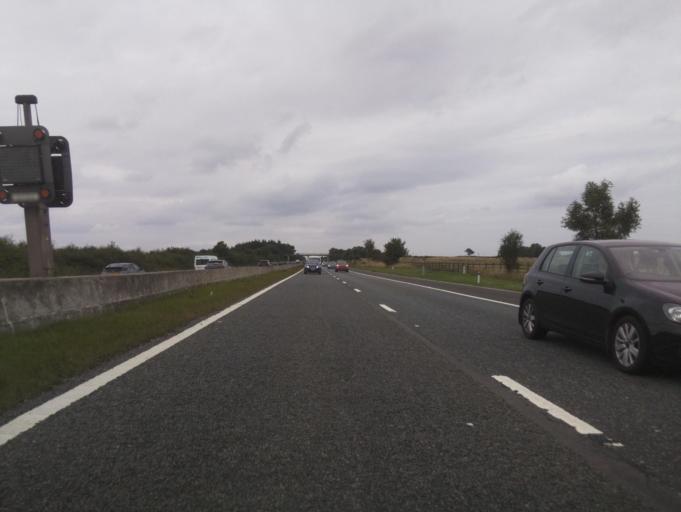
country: GB
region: England
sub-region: County Durham
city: West Rainton
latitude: 54.8239
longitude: -1.5231
